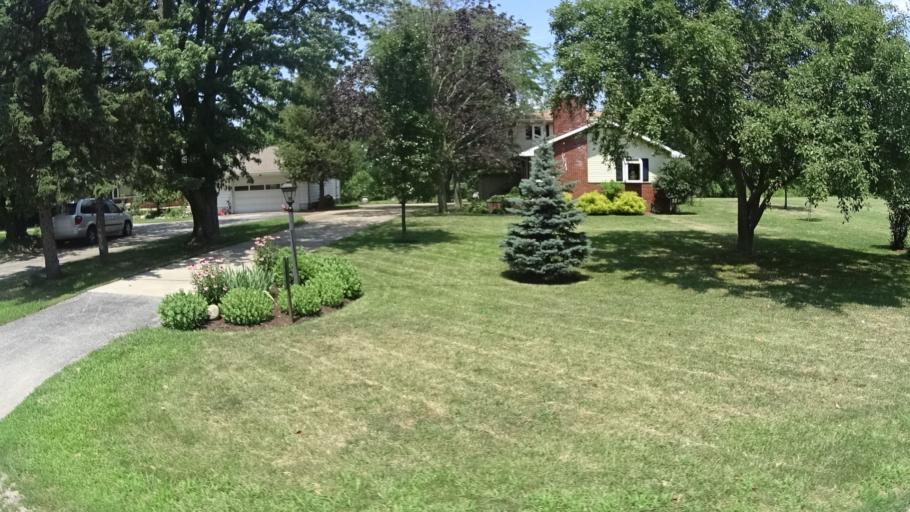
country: US
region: Ohio
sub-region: Erie County
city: Huron
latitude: 41.4130
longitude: -82.6219
